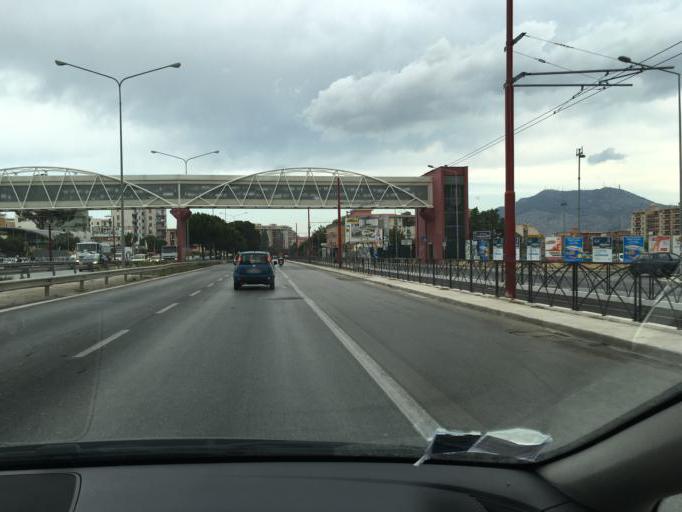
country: IT
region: Sicily
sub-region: Palermo
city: Palermo
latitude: 38.1152
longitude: 13.3294
